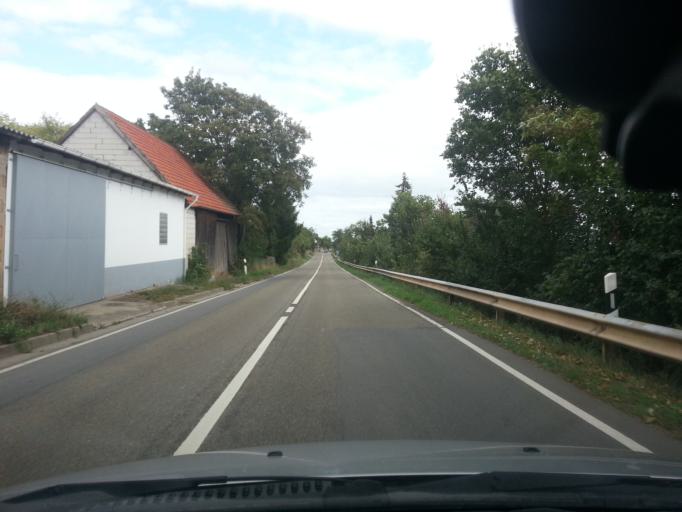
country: DE
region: Rheinland-Pfalz
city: Neuleiningen
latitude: 49.5423
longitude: 8.1323
